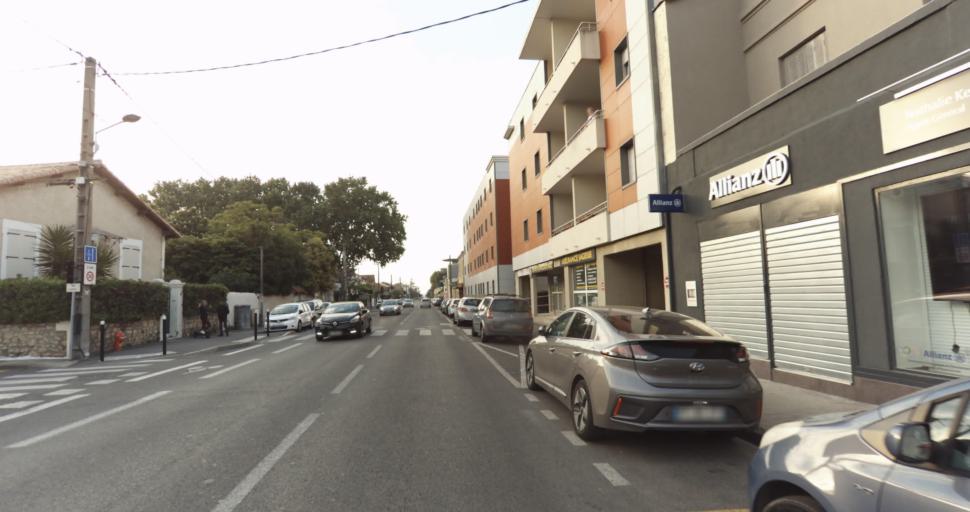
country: FR
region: Languedoc-Roussillon
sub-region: Departement du Gard
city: Nimes
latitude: 43.8294
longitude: 4.3714
